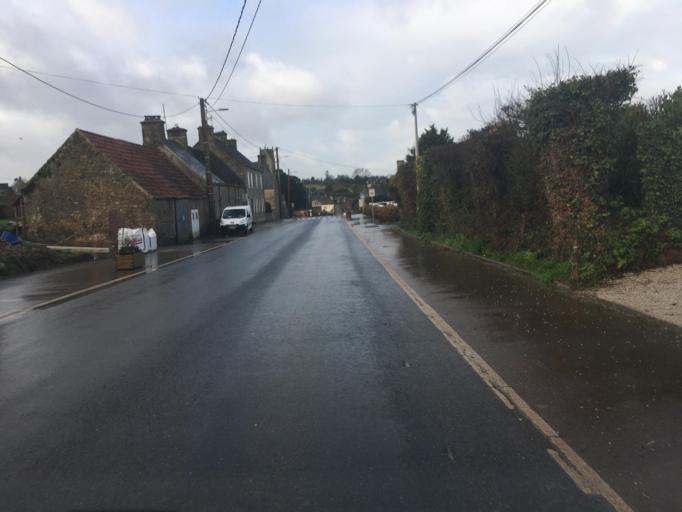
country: FR
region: Lower Normandy
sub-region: Departement de la Manche
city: Saint-Pierre-Eglise
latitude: 49.6707
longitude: -1.3335
